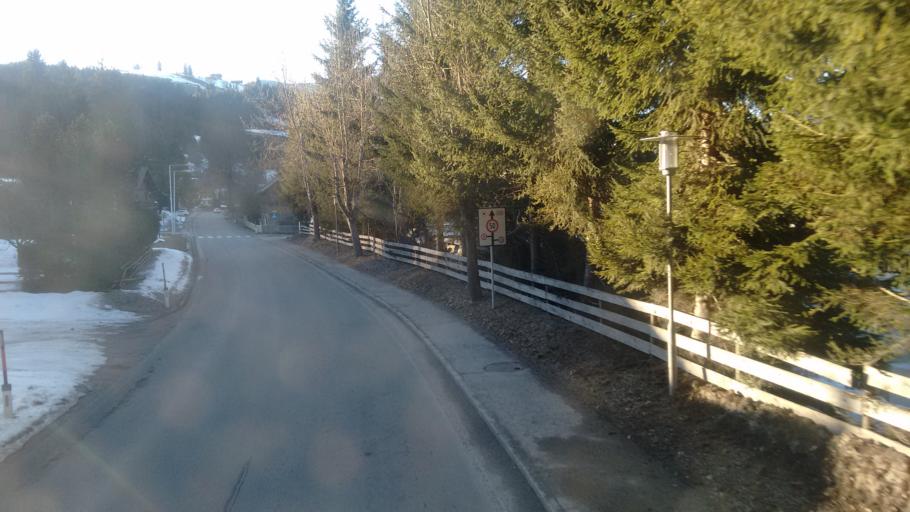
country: AT
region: Salzburg
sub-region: Politischer Bezirk Sankt Johann im Pongau
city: Altenmarkt im Pongau
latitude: 47.3652
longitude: 13.4242
